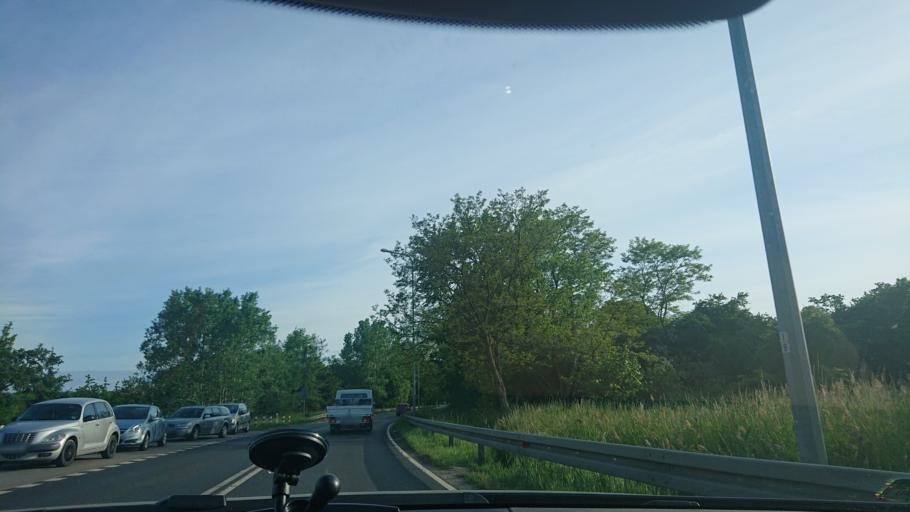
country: PL
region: Greater Poland Voivodeship
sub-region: Powiat gnieznienski
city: Gniezno
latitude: 52.5242
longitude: 17.5856
